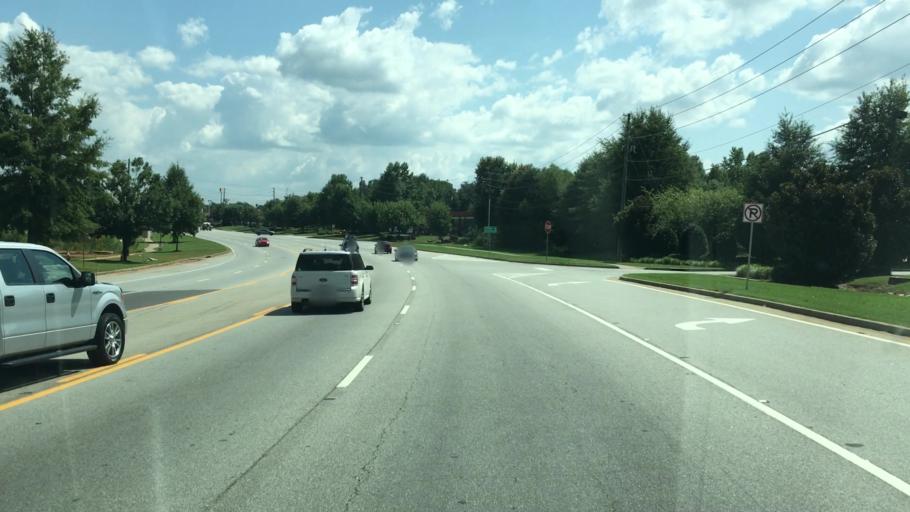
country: US
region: Georgia
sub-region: Morgan County
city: Madison
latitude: 33.5628
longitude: -83.4785
